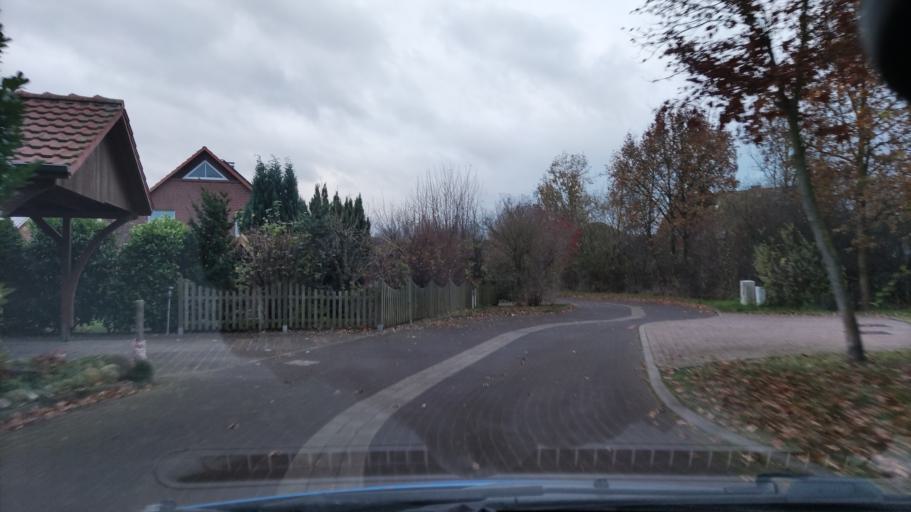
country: DE
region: Lower Saxony
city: Vogelsen
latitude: 53.2728
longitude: 10.3505
